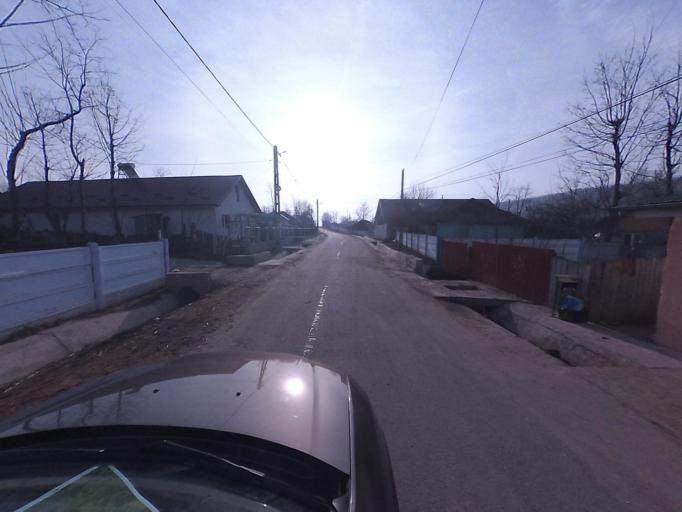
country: RO
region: Vaslui
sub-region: Comuna Solesti
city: Solesti
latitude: 46.8105
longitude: 27.7740
